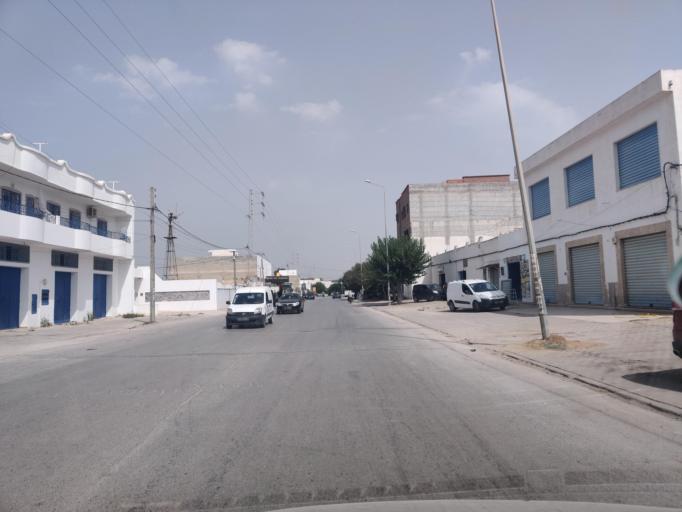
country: TN
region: Nabul
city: Al Hammamat
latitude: 36.4128
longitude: 10.5978
